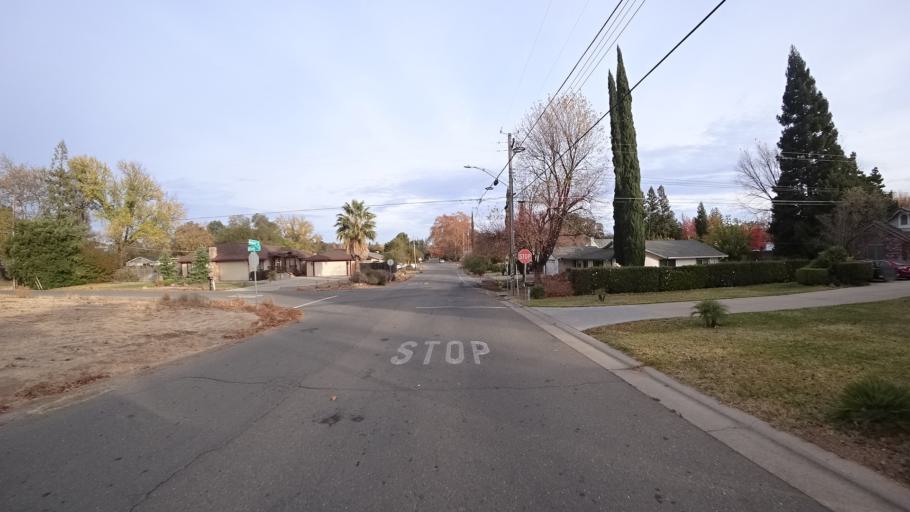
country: US
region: California
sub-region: Sacramento County
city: Citrus Heights
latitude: 38.7137
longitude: -121.2765
